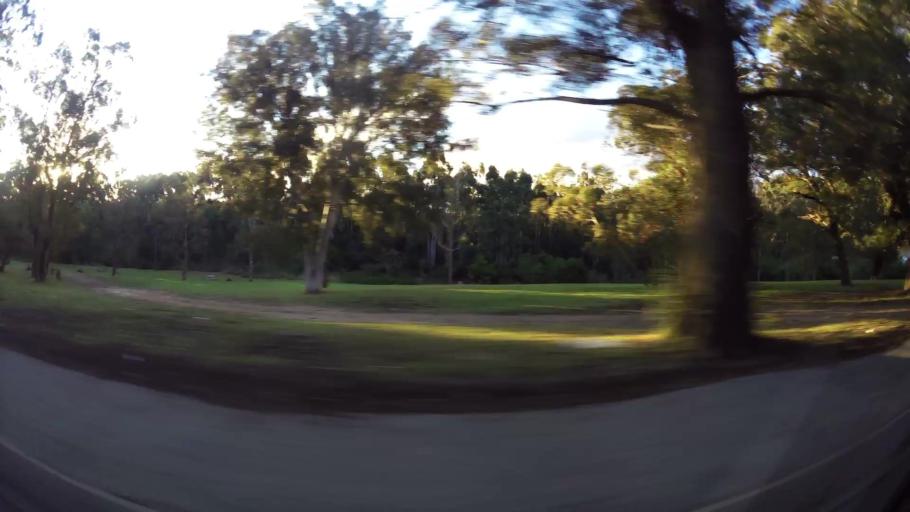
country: ZA
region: Eastern Cape
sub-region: Nelson Mandela Bay Metropolitan Municipality
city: Port Elizabeth
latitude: -33.9601
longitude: 25.5120
